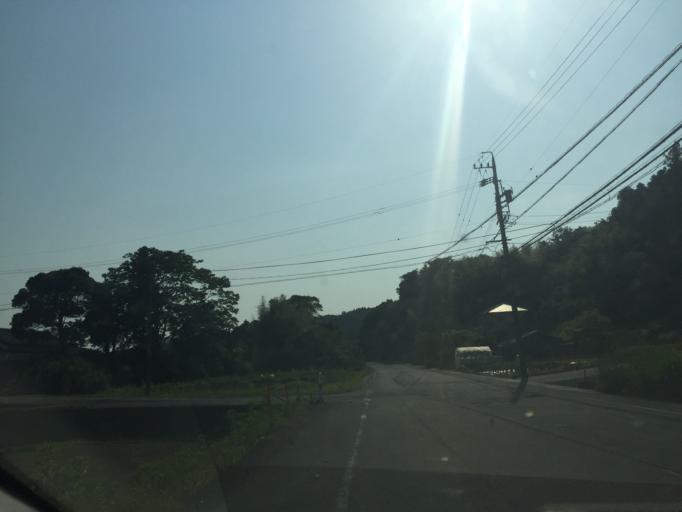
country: JP
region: Shizuoka
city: Kakegawa
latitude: 34.8237
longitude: 138.0398
